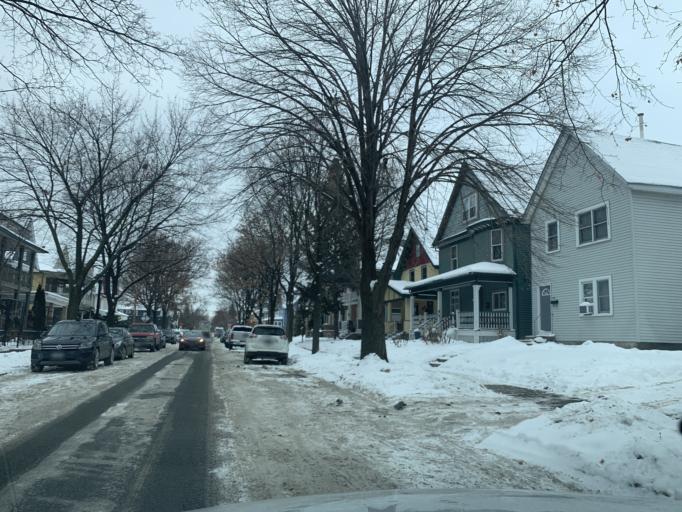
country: US
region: Minnesota
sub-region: Hennepin County
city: Minneapolis
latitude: 44.9567
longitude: -93.2894
